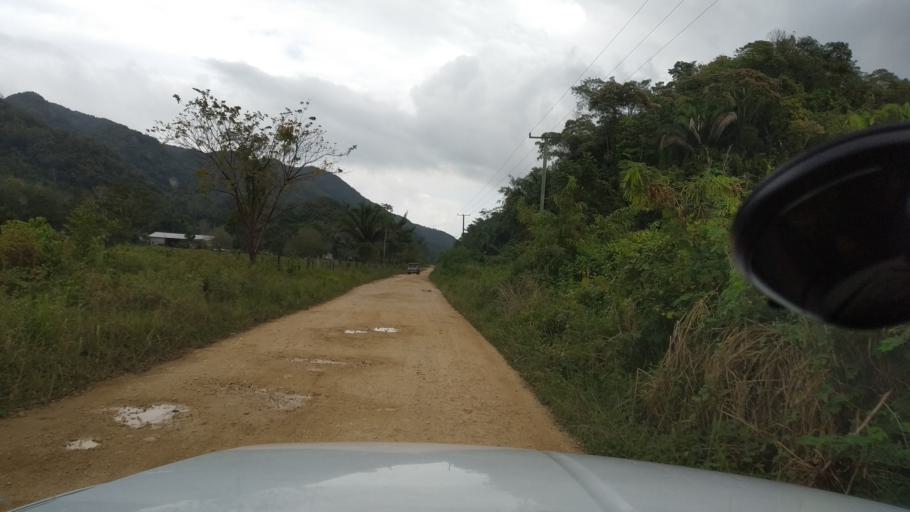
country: BZ
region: Toledo
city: Punta Gorda
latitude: 16.2051
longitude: -89.0307
